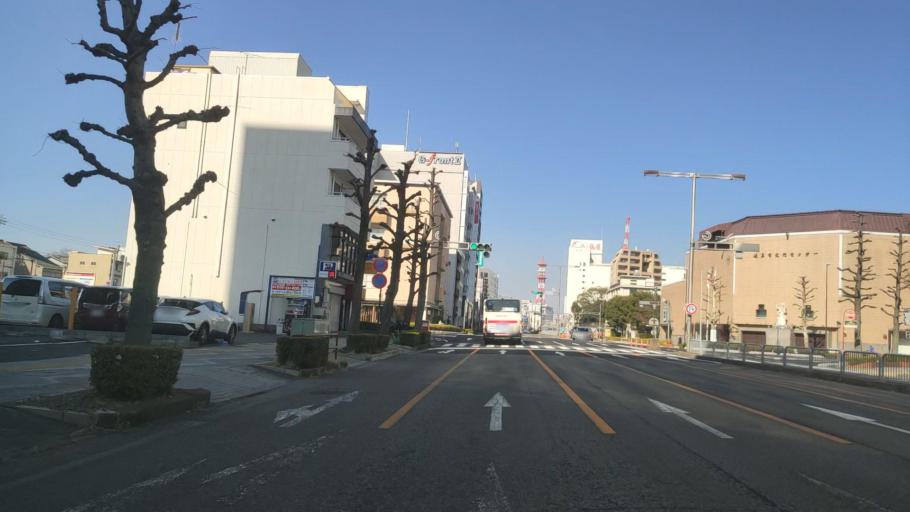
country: JP
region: Gifu
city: Gifu-shi
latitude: 35.4144
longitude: 136.7568
